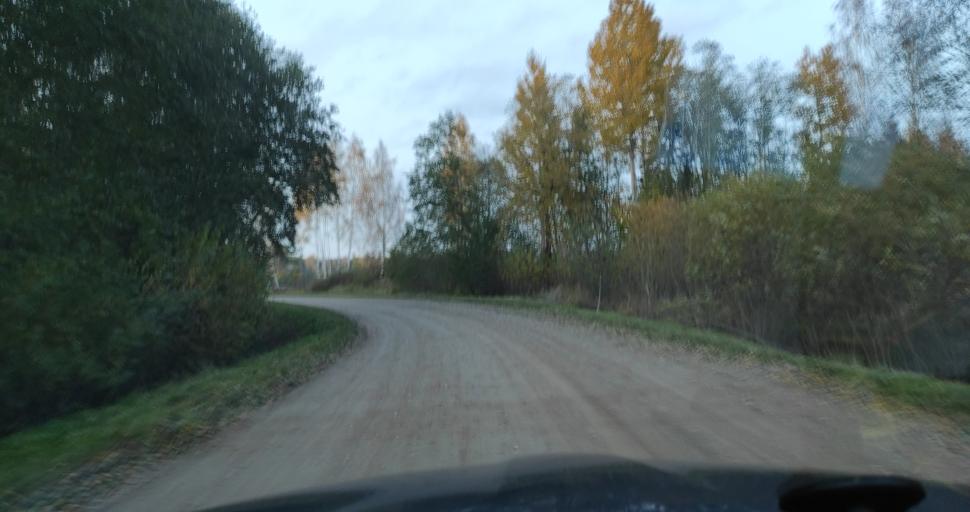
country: LV
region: Aizpute
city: Aizpute
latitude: 56.6670
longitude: 21.7946
